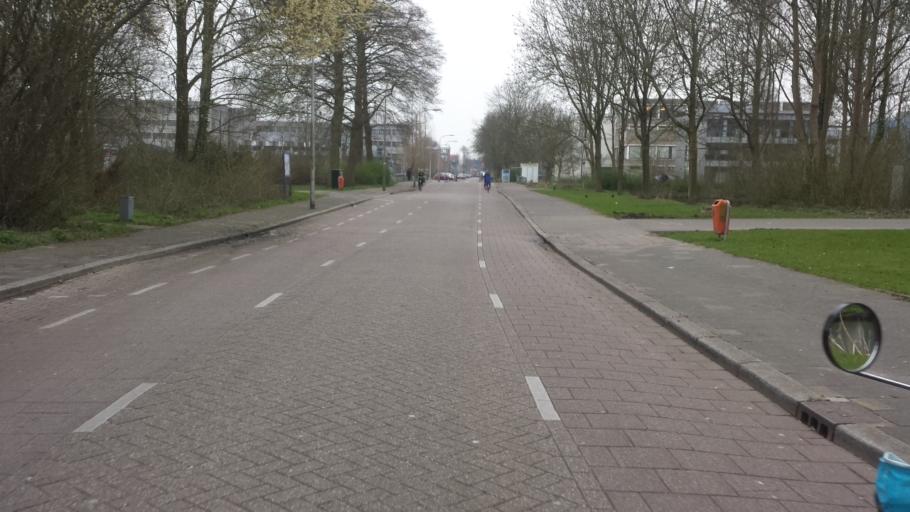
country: NL
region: South Holland
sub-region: Gemeente Gouda
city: Gouda
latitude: 52.0267
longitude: 4.7138
